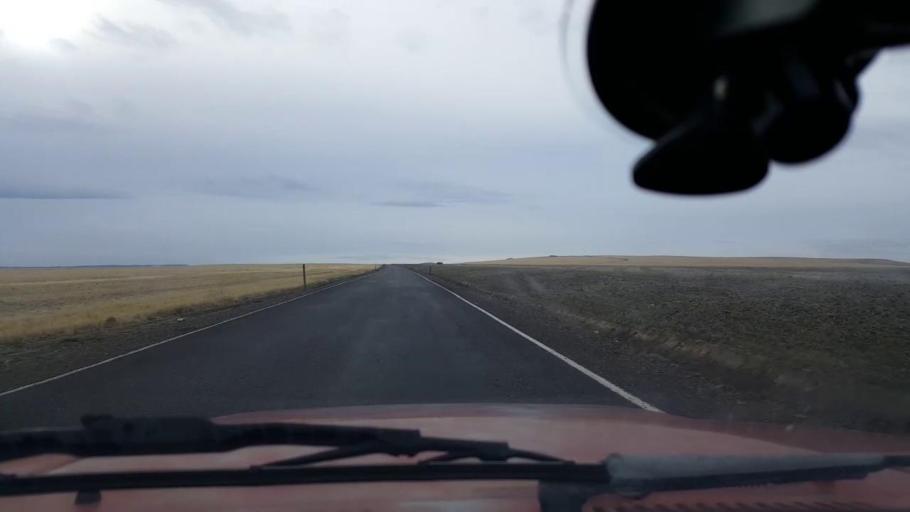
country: US
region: Washington
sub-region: Asotin County
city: Clarkston Heights-Vineland
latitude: 46.3535
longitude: -117.2274
